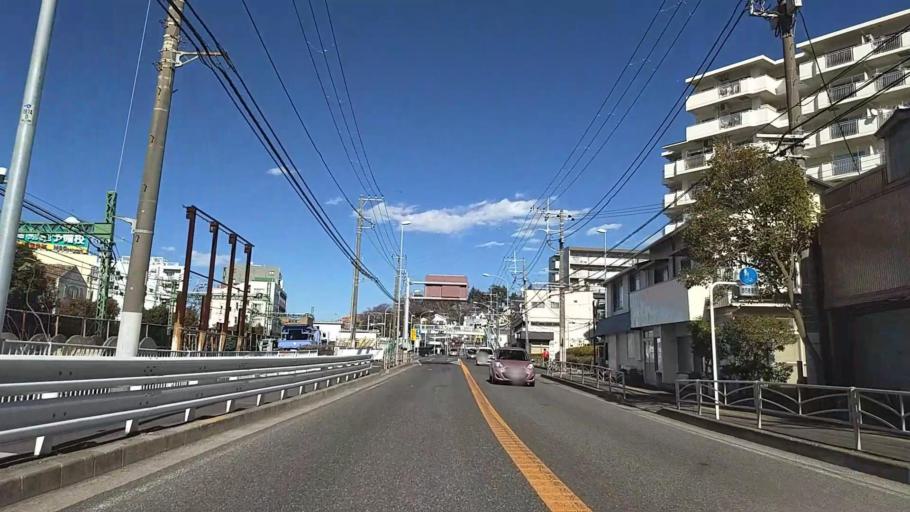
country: JP
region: Kanagawa
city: Zushi
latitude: 35.3586
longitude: 139.6285
